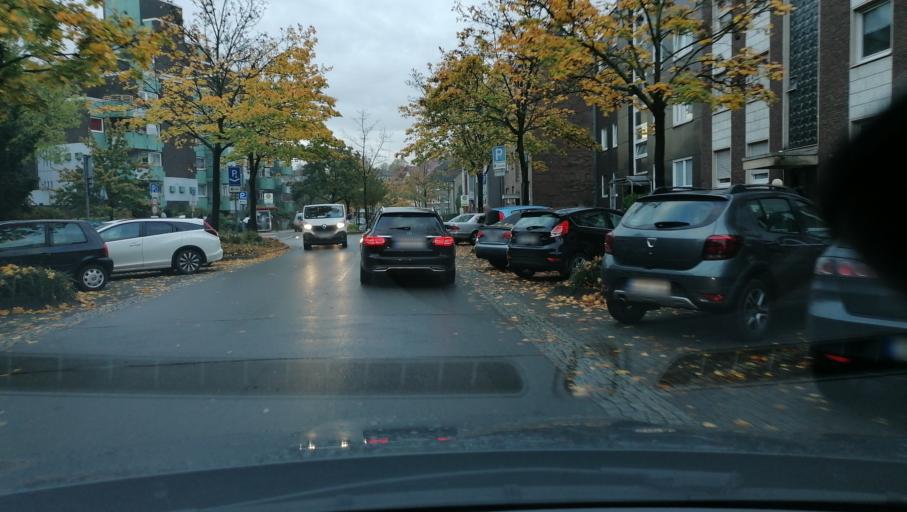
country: DE
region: North Rhine-Westphalia
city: Herten
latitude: 51.5923
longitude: 7.1377
